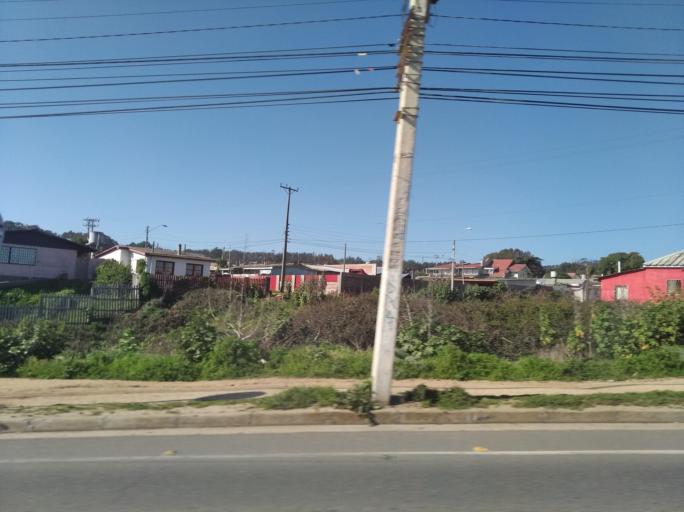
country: CL
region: Valparaiso
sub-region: San Antonio Province
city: El Tabo
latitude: -33.4528
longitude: -71.6729
